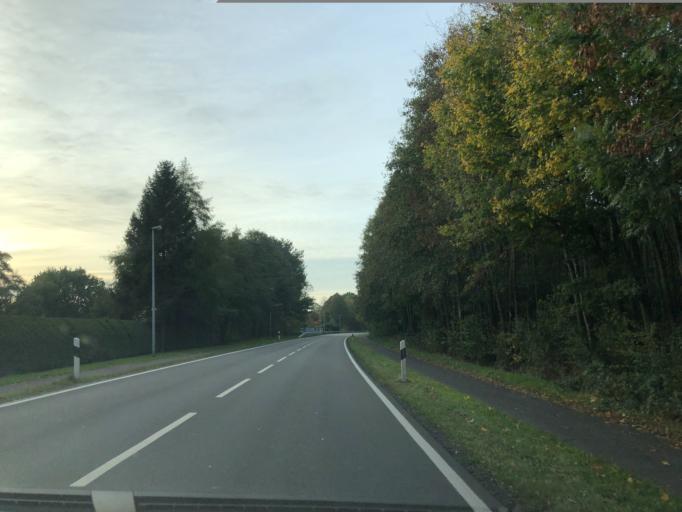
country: DE
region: Lower Saxony
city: Papenburg
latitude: 53.0640
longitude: 7.4041
